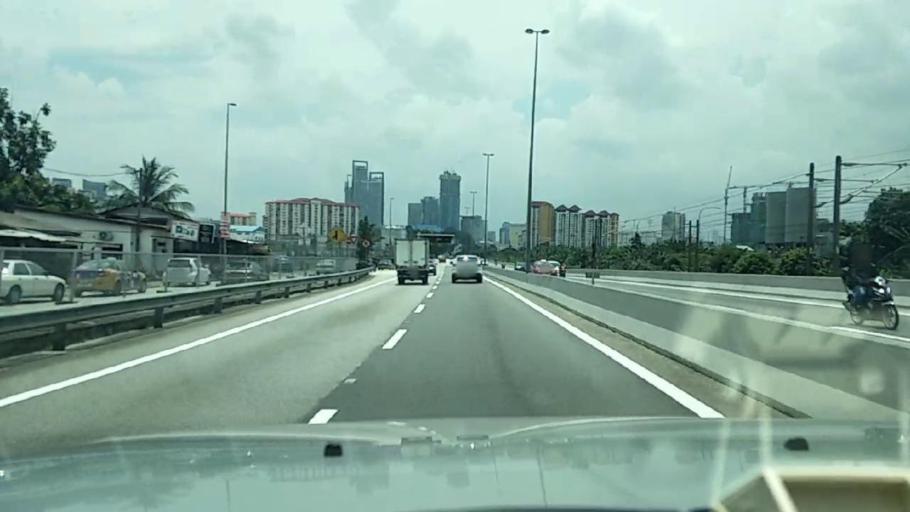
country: MY
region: Kuala Lumpur
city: Kuala Lumpur
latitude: 3.0988
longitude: 101.6705
